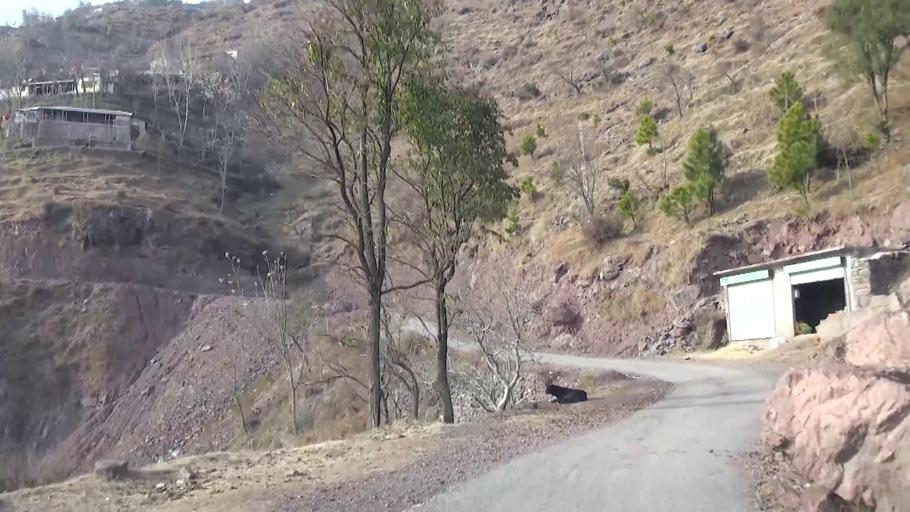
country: PK
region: Azad Kashmir
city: Muzaffarabad
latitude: 34.3694
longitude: 73.5238
